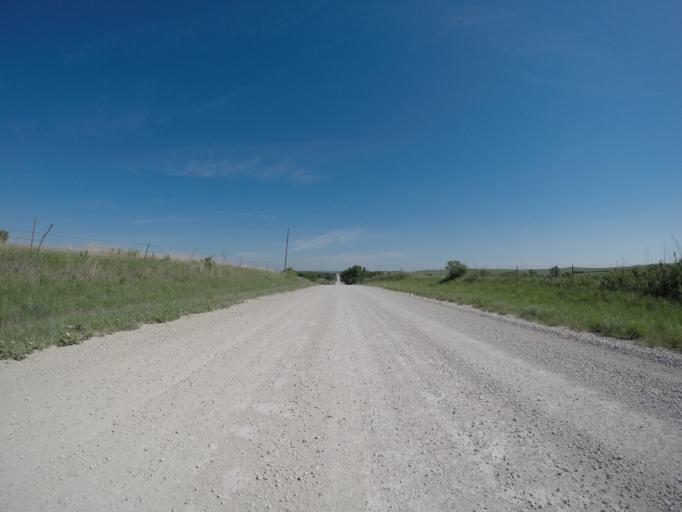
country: US
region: Kansas
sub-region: Wabaunsee County
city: Alma
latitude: 38.9866
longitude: -96.1139
